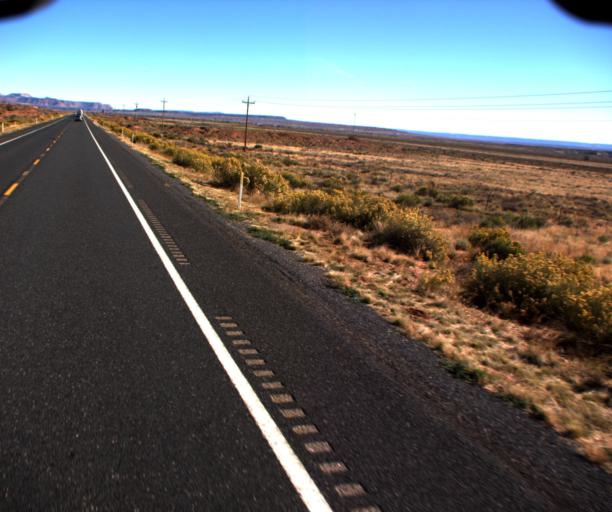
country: US
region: Arizona
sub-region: Coconino County
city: Fredonia
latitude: 36.9126
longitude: -112.5841
